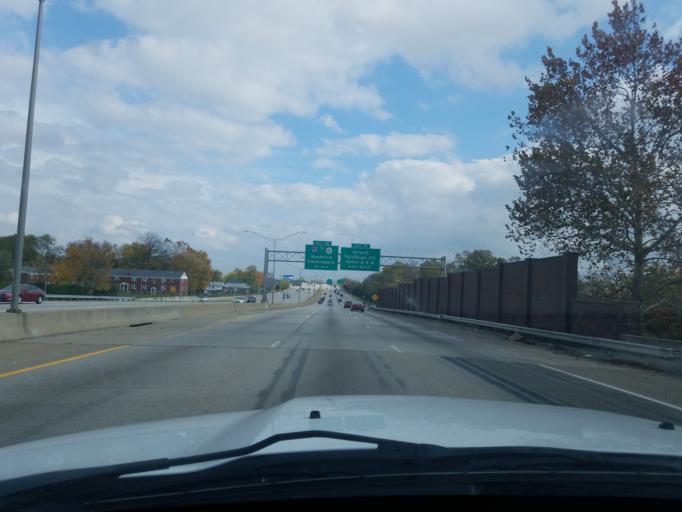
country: US
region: Kentucky
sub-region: Jefferson County
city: Audubon Park
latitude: 38.1899
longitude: -85.7649
